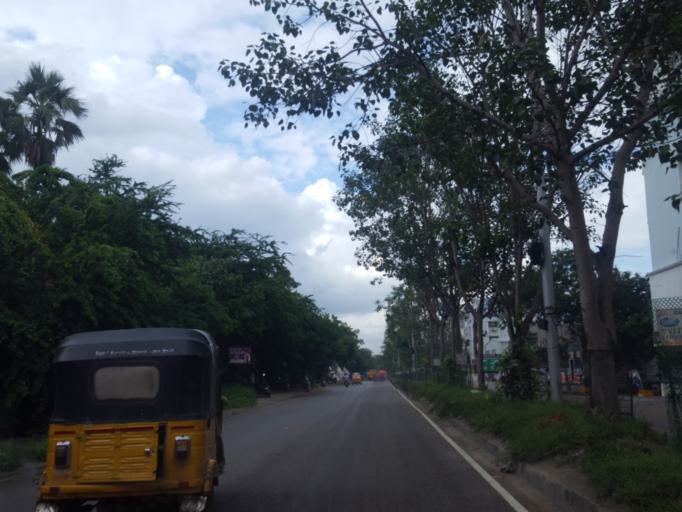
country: IN
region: Telangana
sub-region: Medak
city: Serilingampalle
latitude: 17.4874
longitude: 78.3134
